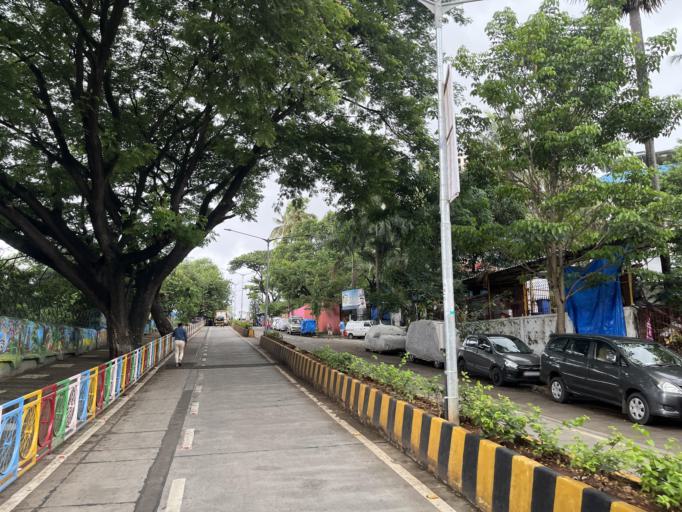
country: IN
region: Maharashtra
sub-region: Mumbai Suburban
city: Borivli
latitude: 19.2330
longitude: 72.8697
